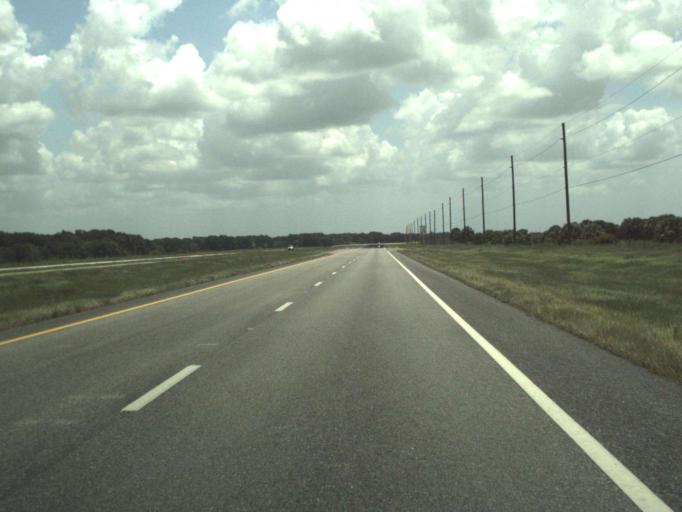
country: US
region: Florida
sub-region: Saint Lucie County
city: Fort Pierce South
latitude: 27.3735
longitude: -80.5822
